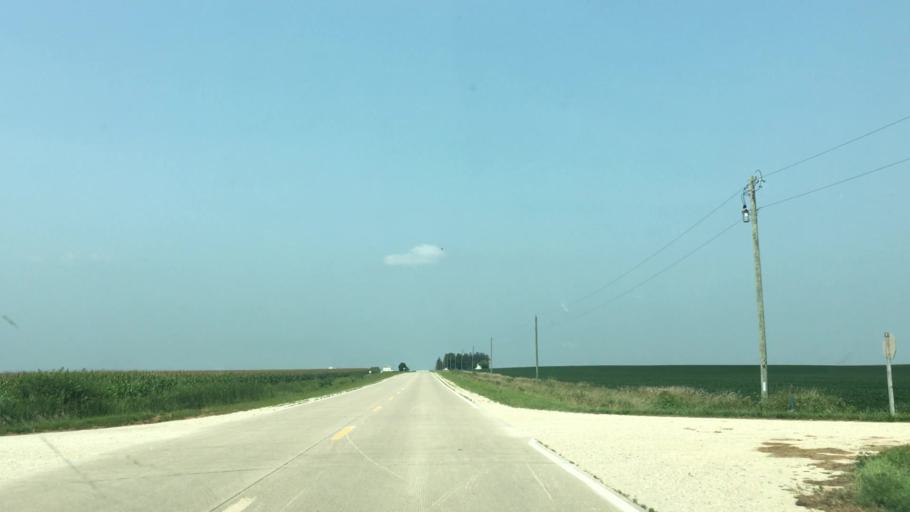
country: US
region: Iowa
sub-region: Fayette County
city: Oelwein
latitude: 42.7020
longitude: -91.8048
